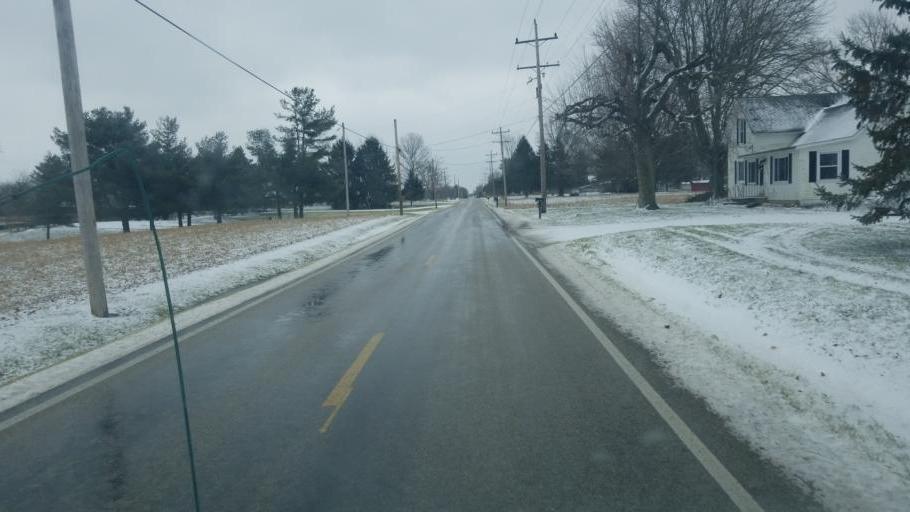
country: US
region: Ohio
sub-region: Delaware County
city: Sunbury
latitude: 40.2473
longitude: -82.7785
